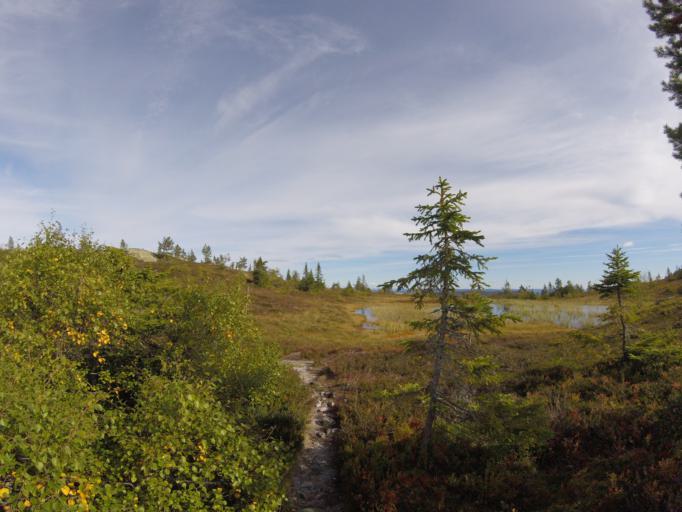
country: NO
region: Buskerud
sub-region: Flesberg
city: Lampeland
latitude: 59.7491
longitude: 9.4184
